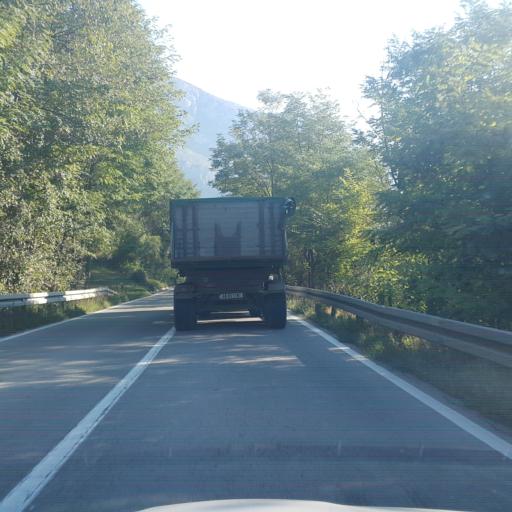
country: RS
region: Central Serbia
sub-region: Nisavski Okrug
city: Svrljig
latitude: 43.3293
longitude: 22.1136
